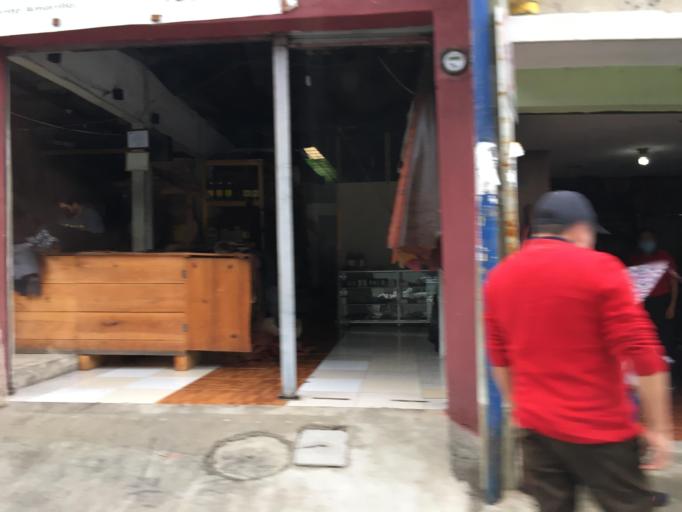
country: GT
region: Sacatepequez
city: Pastores
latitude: 14.5936
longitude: -90.7527
